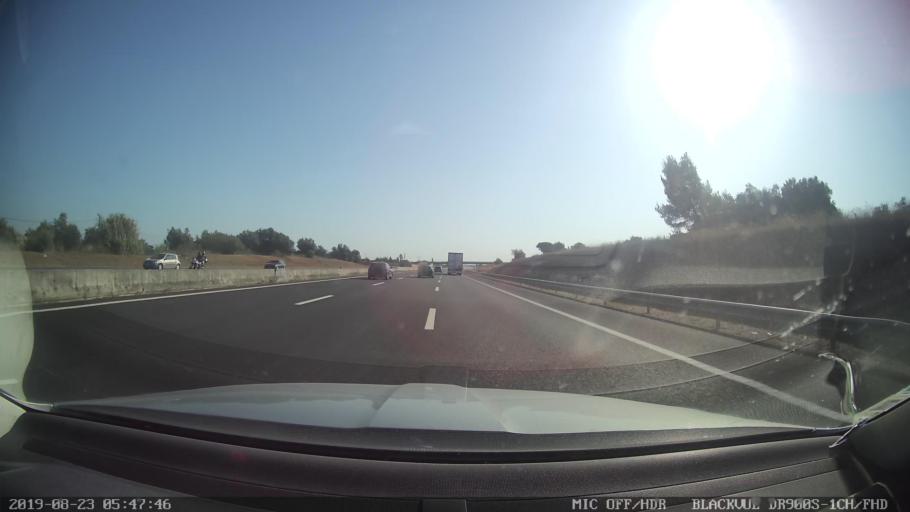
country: PT
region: Santarem
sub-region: Cartaxo
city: Pontevel
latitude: 39.1815
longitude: -8.8309
